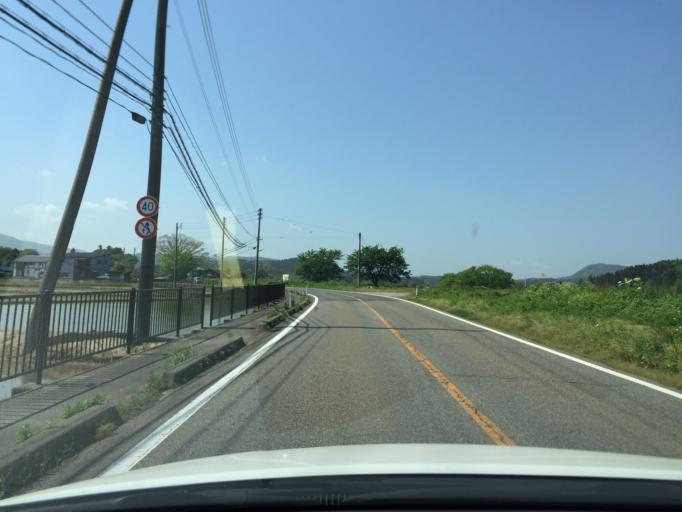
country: JP
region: Niigata
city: Muramatsu
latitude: 37.6808
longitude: 139.1498
